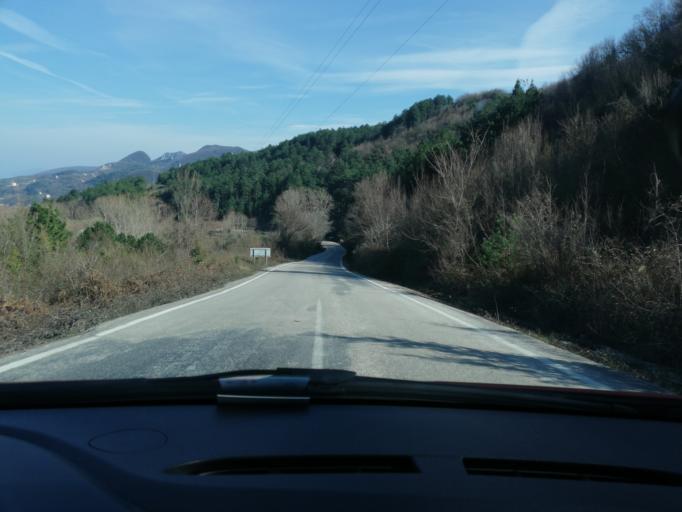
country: TR
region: Bartin
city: Kurucasile
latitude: 41.8335
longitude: 32.6960
